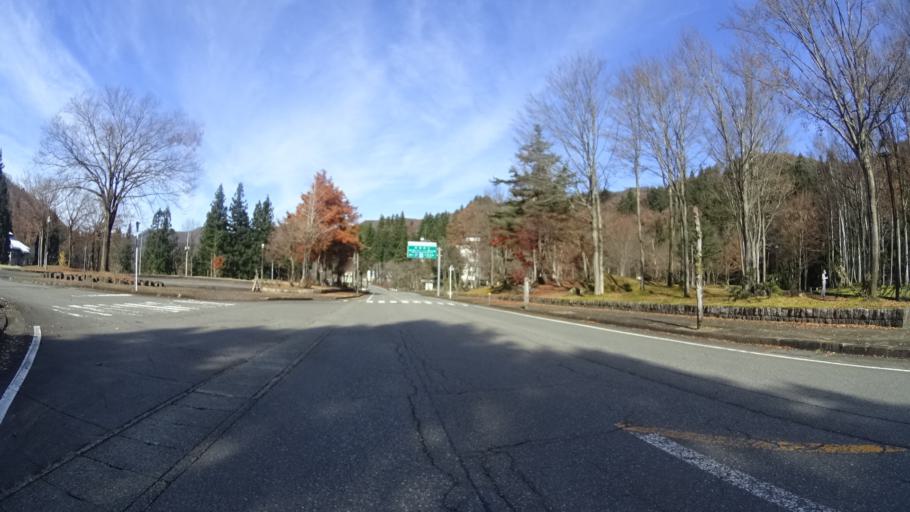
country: JP
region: Niigata
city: Muikamachi
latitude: 37.1977
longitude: 139.0768
